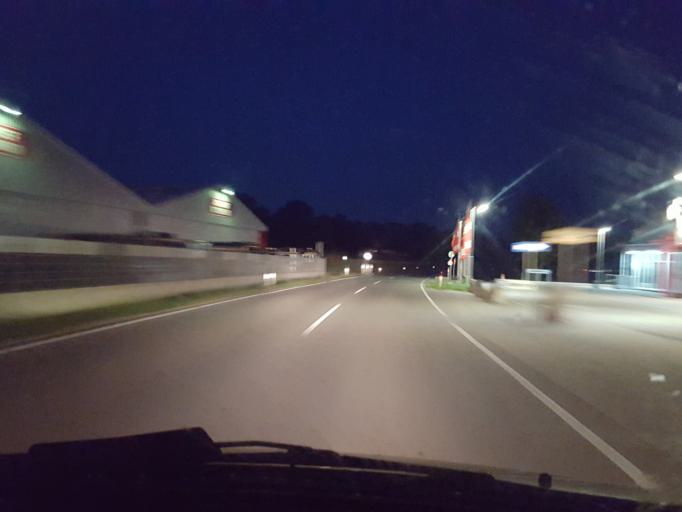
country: AT
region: Lower Austria
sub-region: Politischer Bezirk Scheibbs
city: Purgstall
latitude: 48.0597
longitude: 15.1492
